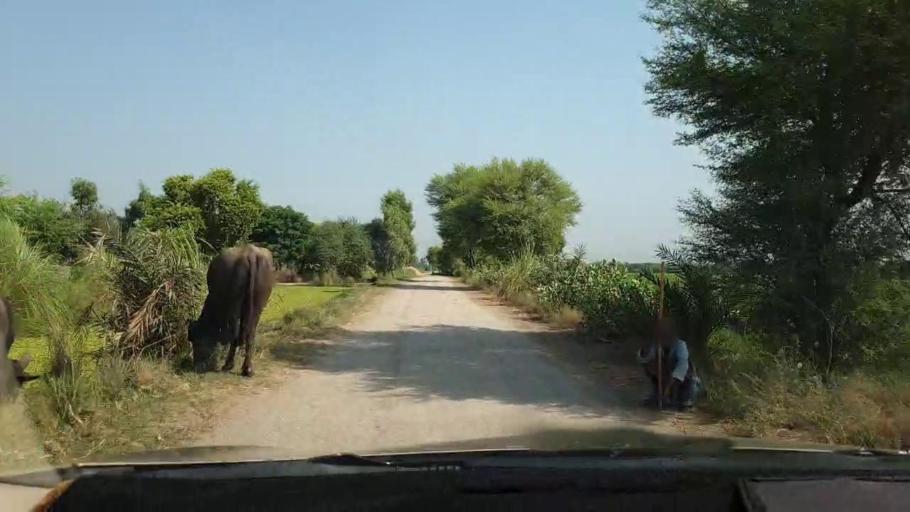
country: PK
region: Sindh
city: Larkana
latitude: 27.6354
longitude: 68.2370
